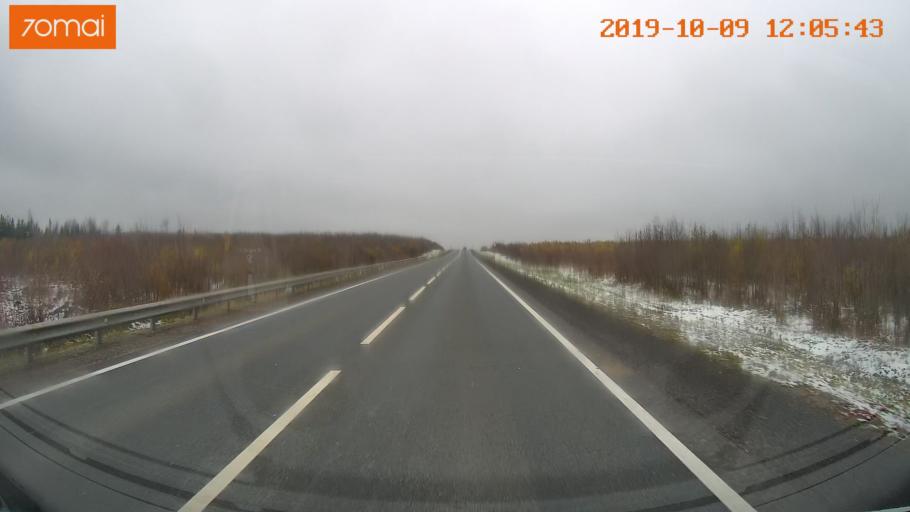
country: RU
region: Jaroslavl
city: Prechistoye
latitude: 58.6253
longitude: 40.3303
